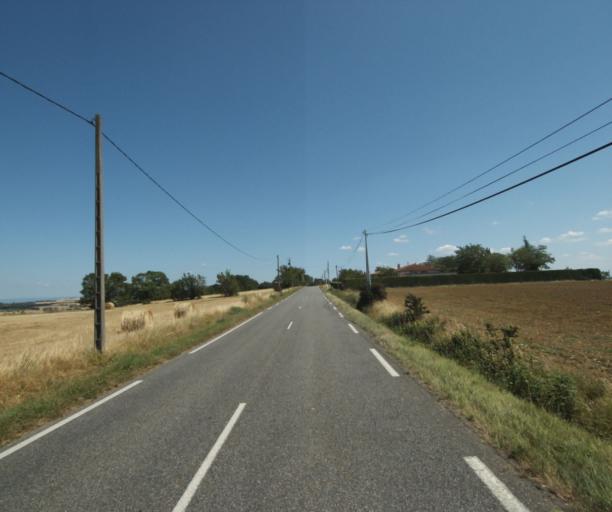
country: FR
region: Midi-Pyrenees
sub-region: Departement de la Haute-Garonne
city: Saint-Felix-Lauragais
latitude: 43.5011
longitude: 1.8799
